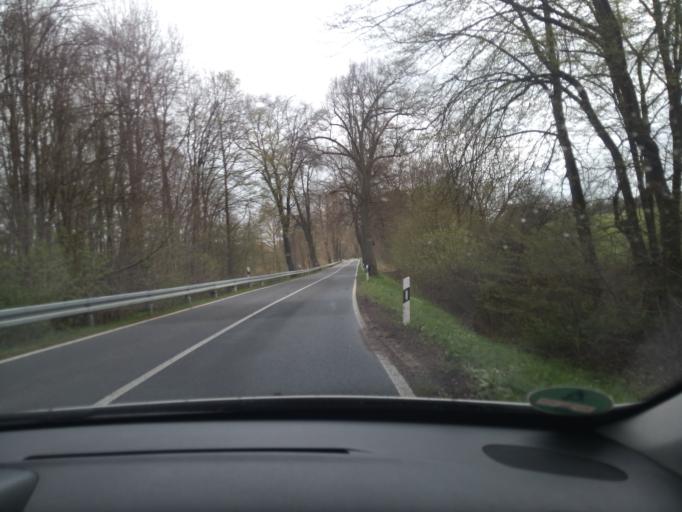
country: DE
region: Mecklenburg-Vorpommern
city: Loitz
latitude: 53.3394
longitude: 13.4155
